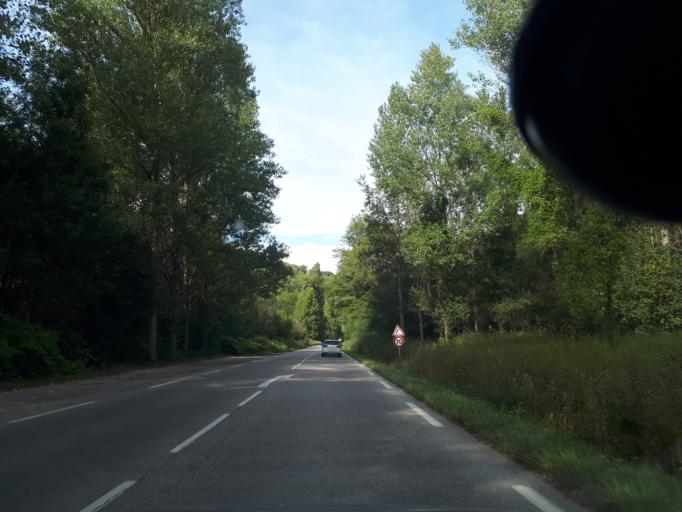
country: FR
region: Rhone-Alpes
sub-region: Departement de l'Isere
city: Maubec
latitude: 45.5604
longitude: 5.2750
